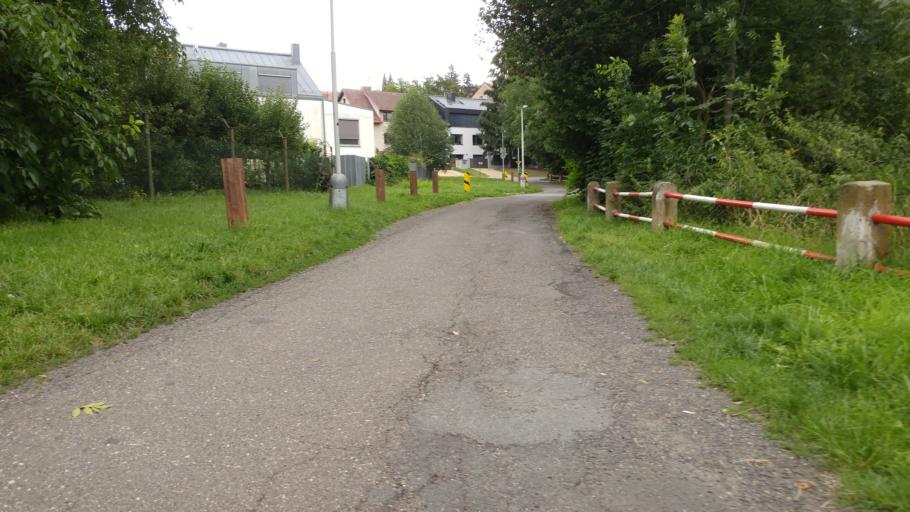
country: CZ
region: Praha
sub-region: Praha 14
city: Hostavice
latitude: 50.0494
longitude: 14.5320
